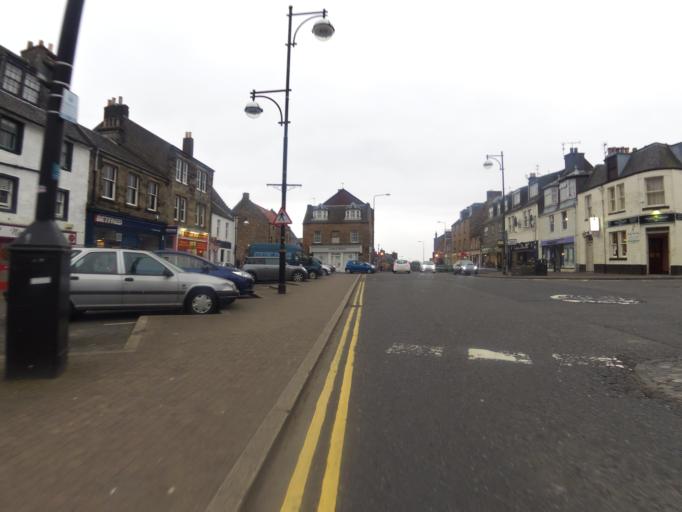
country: GB
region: Scotland
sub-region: Fife
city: Inverkeithing
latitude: 56.0304
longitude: -3.3982
